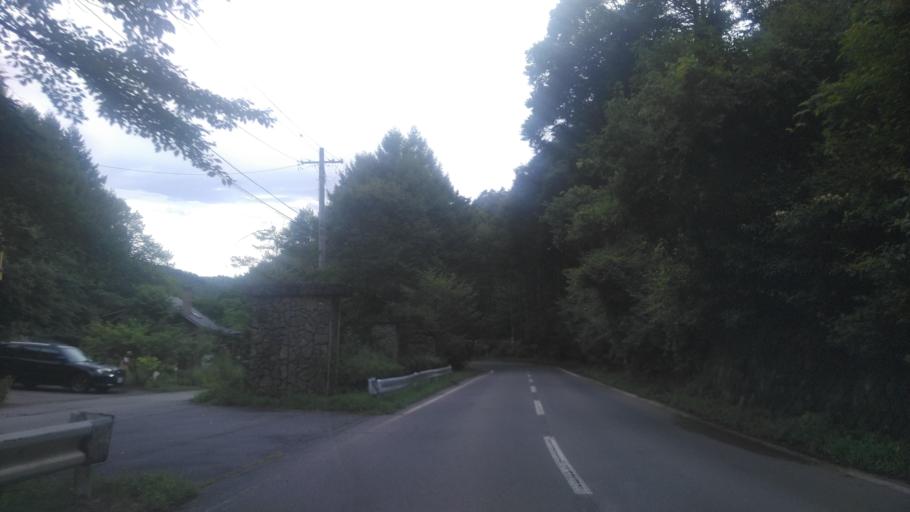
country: JP
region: Nagano
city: Ueda
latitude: 36.5036
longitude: 138.2306
